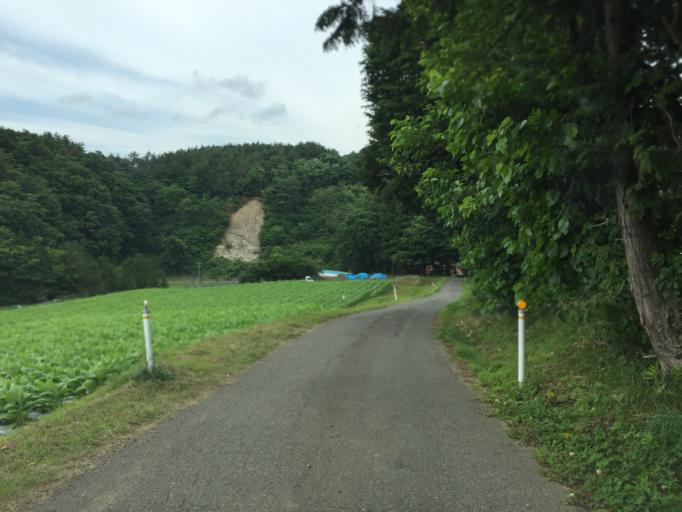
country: JP
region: Fukushima
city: Funehikimachi-funehiki
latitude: 37.4120
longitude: 140.7007
